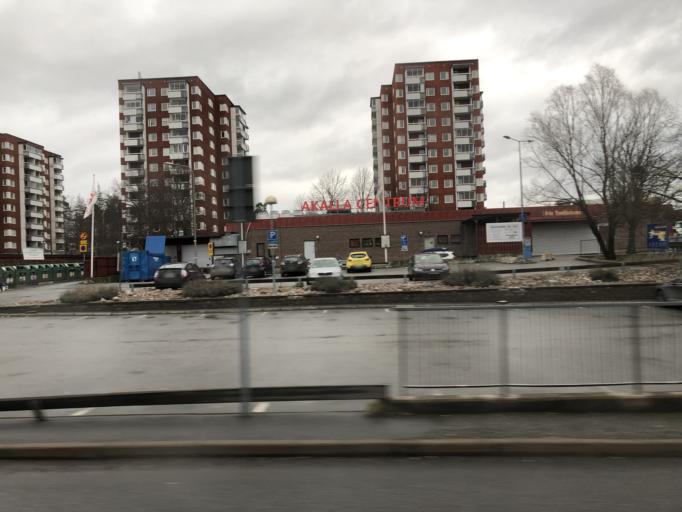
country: SE
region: Stockholm
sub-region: Stockholms Kommun
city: Kista
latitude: 59.4148
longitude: 17.9113
